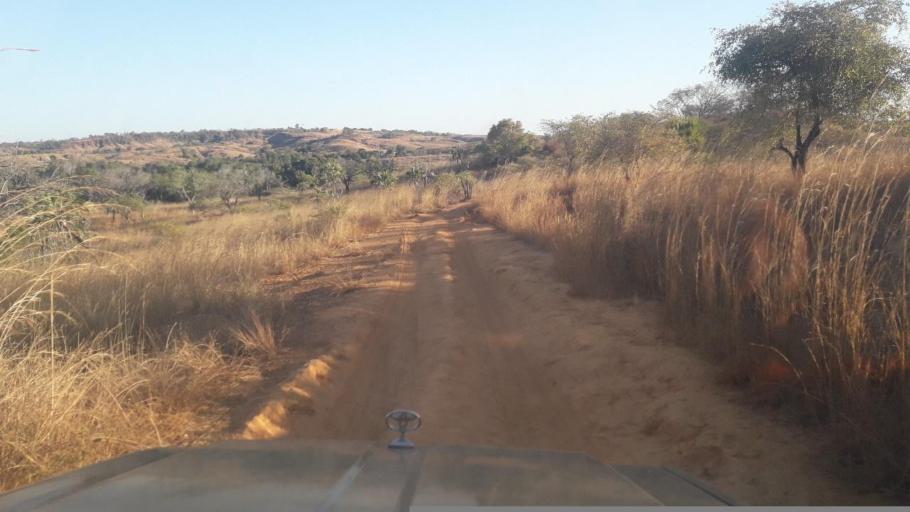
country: MG
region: Boeny
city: Sitampiky
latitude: -16.5047
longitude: 45.6010
